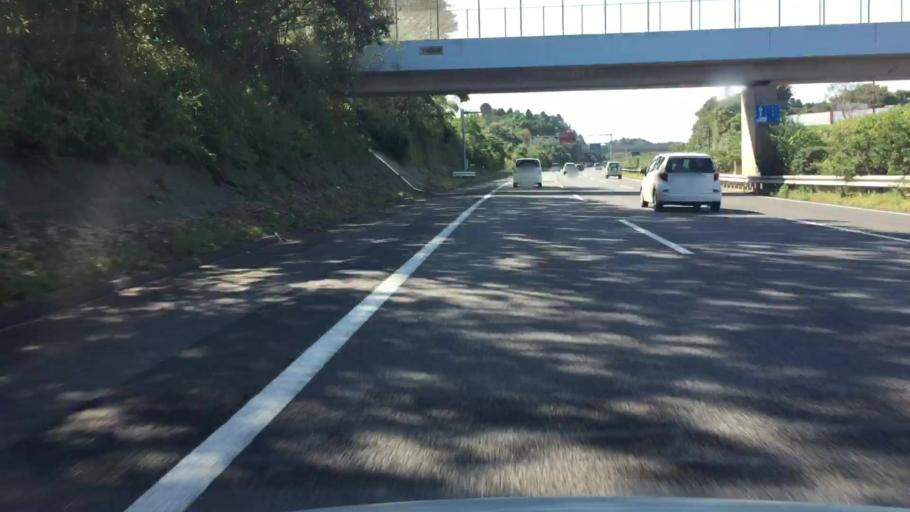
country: JP
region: Ibaraki
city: Naka
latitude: 36.0630
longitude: 140.1577
